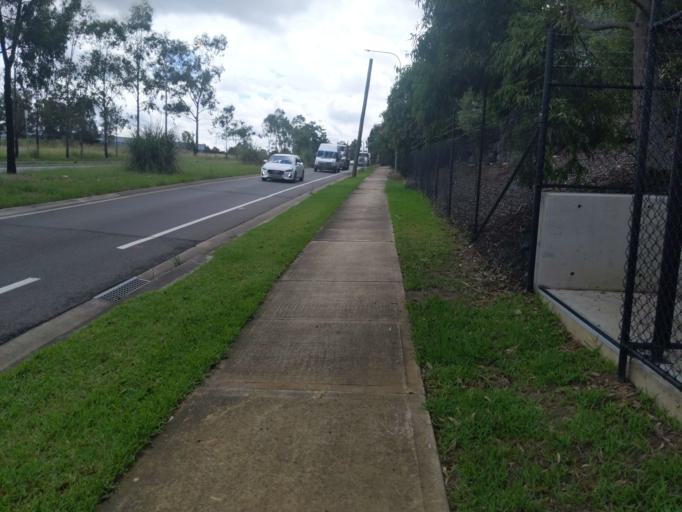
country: AU
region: New South Wales
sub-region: Holroyd
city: Girraween
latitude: -33.8184
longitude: 150.9195
